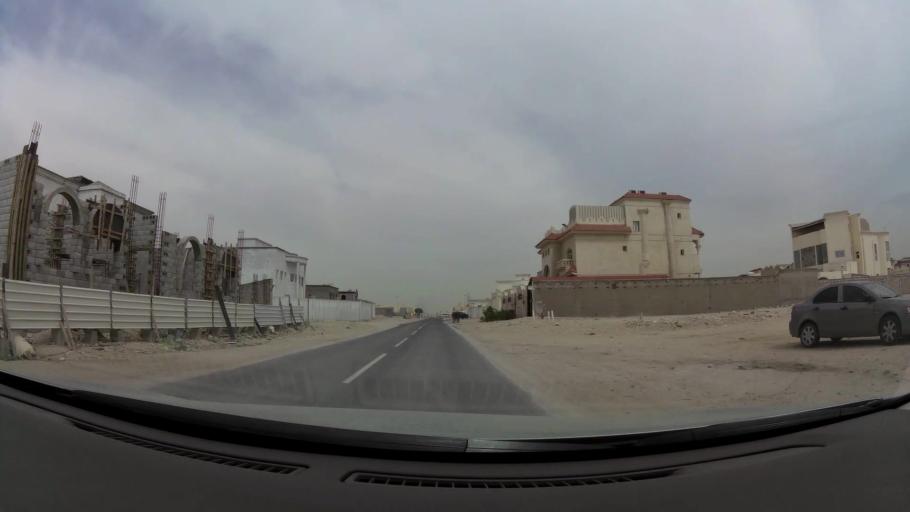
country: QA
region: Baladiyat ar Rayyan
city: Ar Rayyan
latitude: 25.2188
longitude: 51.4631
